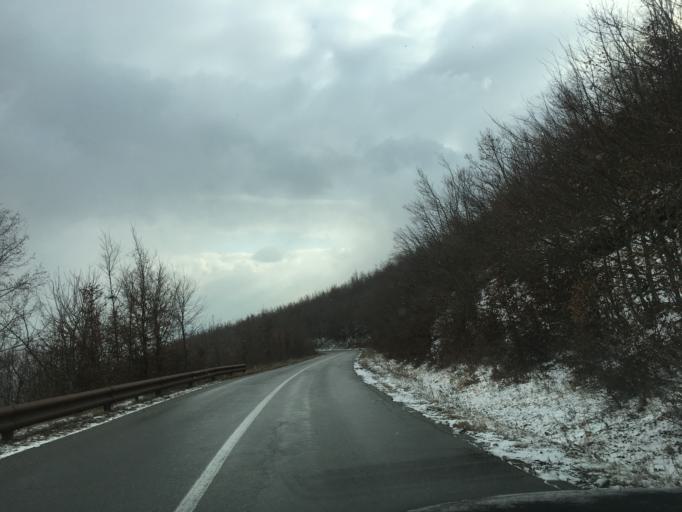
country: XK
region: Pec
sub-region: Komuna e Pejes
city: Dubova (Driloni)
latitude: 42.7527
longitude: 20.3015
